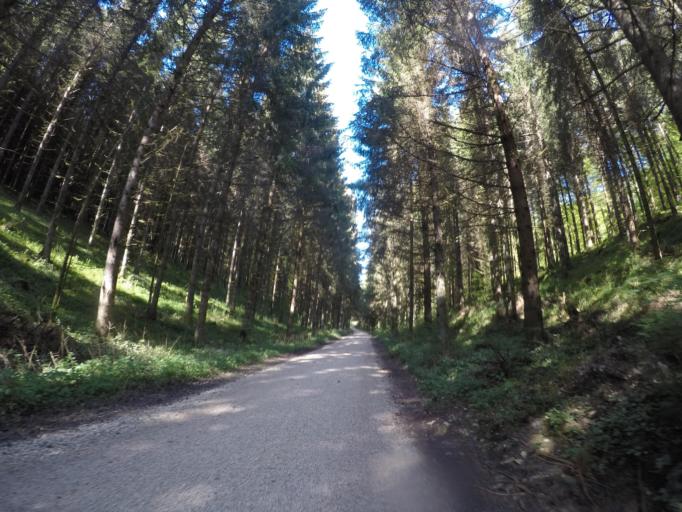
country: DE
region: Baden-Wuerttemberg
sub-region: Tuebingen Region
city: Berghulen
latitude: 48.4858
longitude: 9.7717
